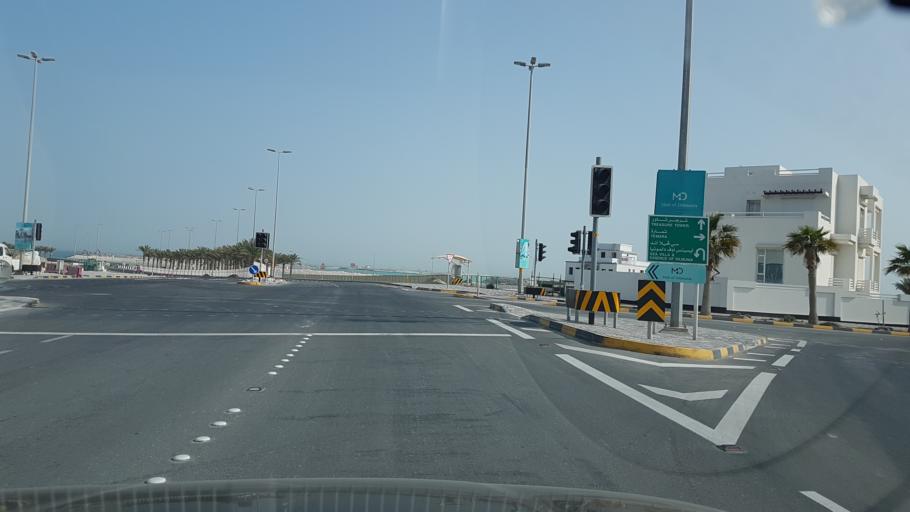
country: BH
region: Muharraq
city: Al Hadd
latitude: 26.2692
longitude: 50.6709
